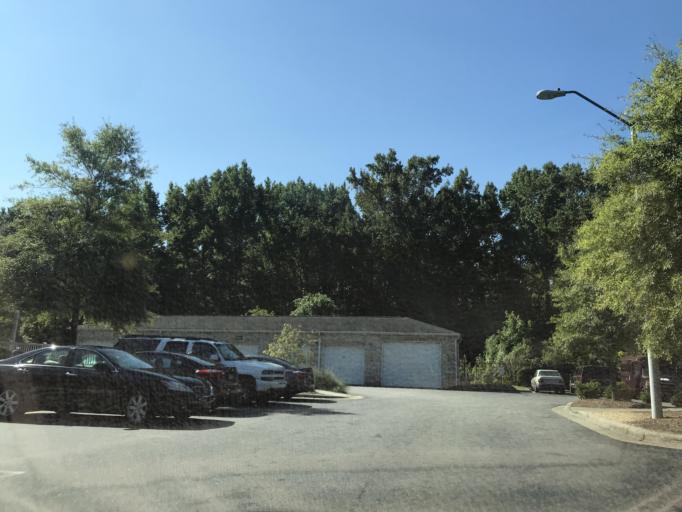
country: US
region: North Carolina
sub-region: Wake County
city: Raleigh
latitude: 35.7919
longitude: -78.5830
